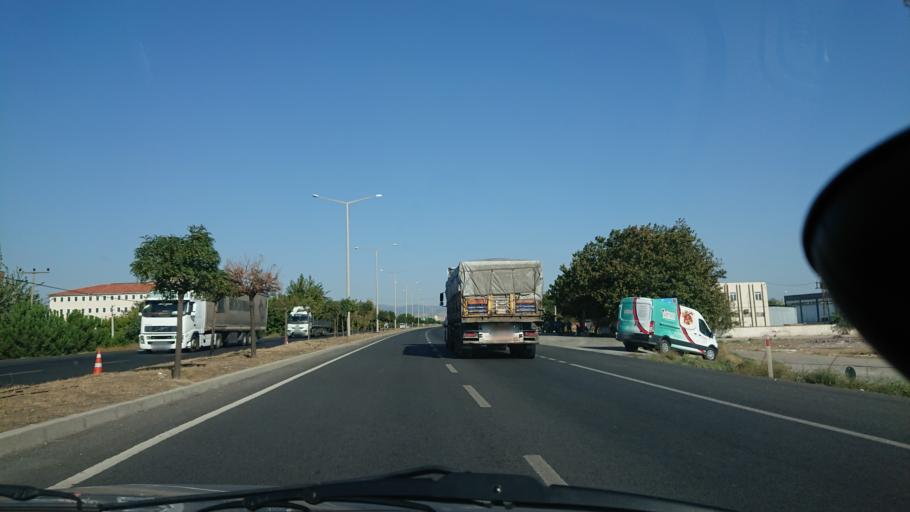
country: TR
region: Manisa
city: Adala
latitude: 38.5092
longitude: 28.2489
